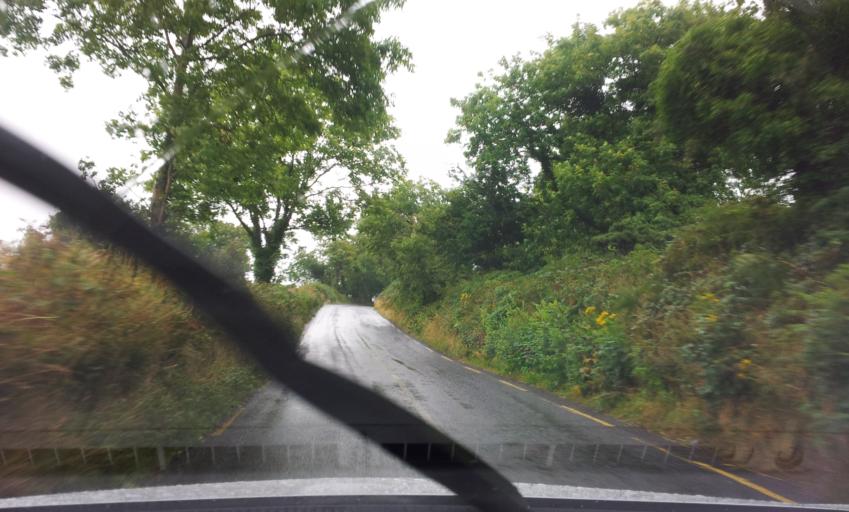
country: IE
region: Leinster
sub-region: Loch Garman
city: New Ross
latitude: 52.4077
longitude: -7.0439
